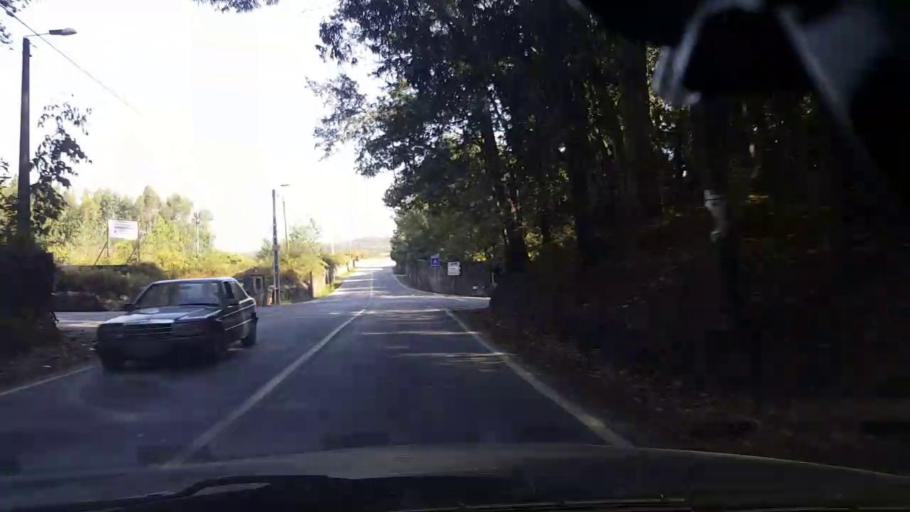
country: PT
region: Porto
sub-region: Vila do Conde
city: Arvore
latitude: 41.3626
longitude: -8.6739
